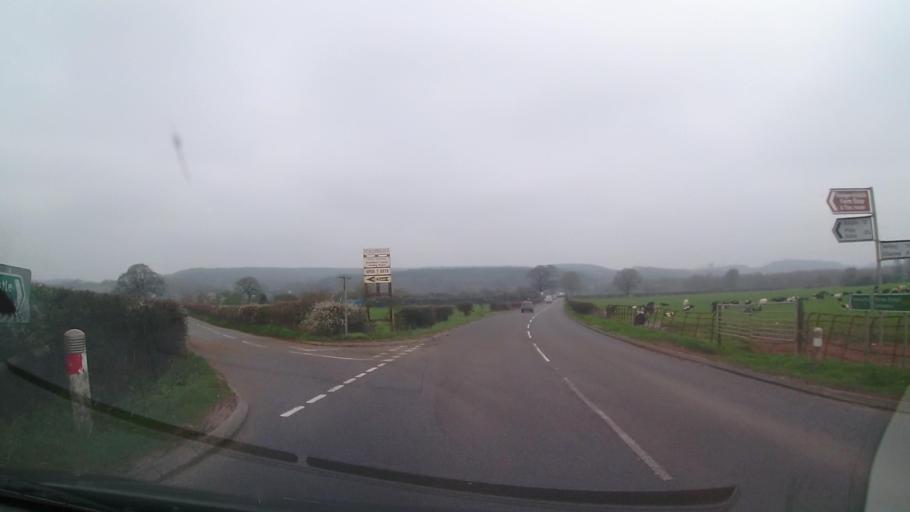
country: GB
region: England
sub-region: Staffordshire
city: Standon
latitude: 52.9398
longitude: -2.3526
